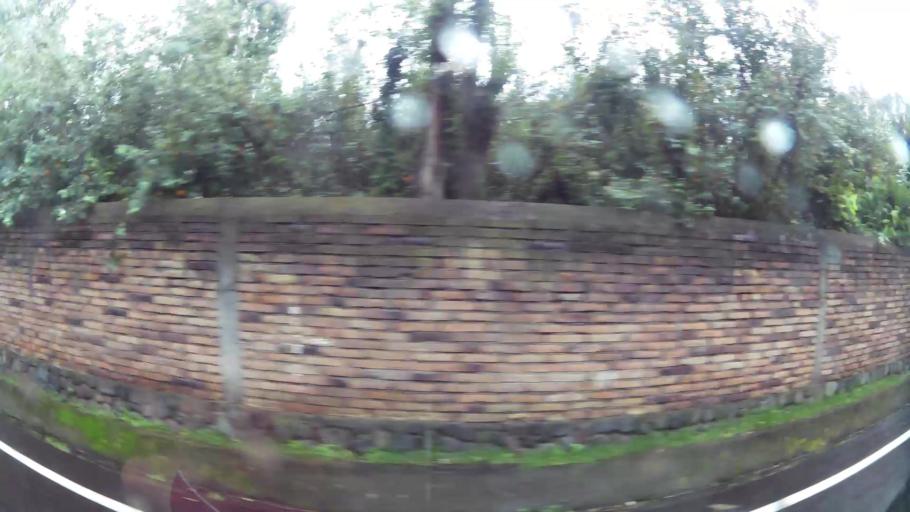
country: EC
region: Pichincha
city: Sangolqui
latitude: -0.2834
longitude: -78.4439
